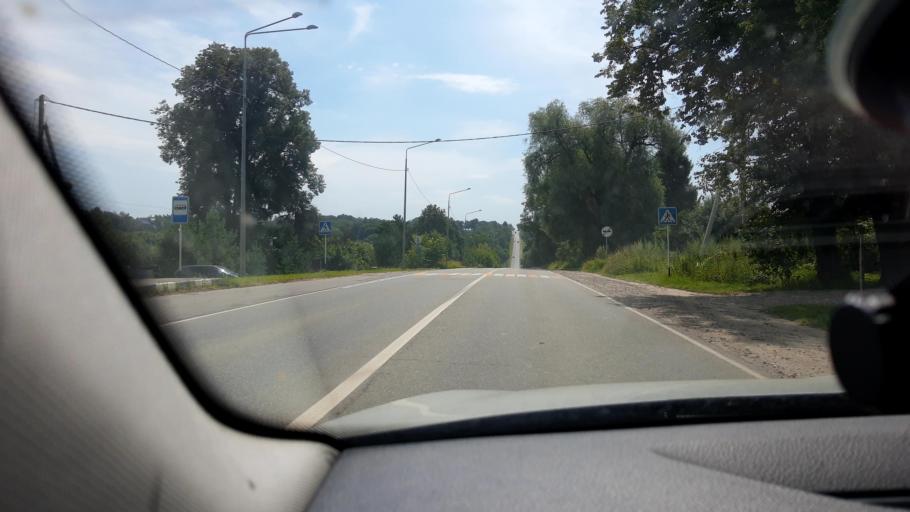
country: RU
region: Tula
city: Zaokskiy
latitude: 54.7606
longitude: 37.4373
